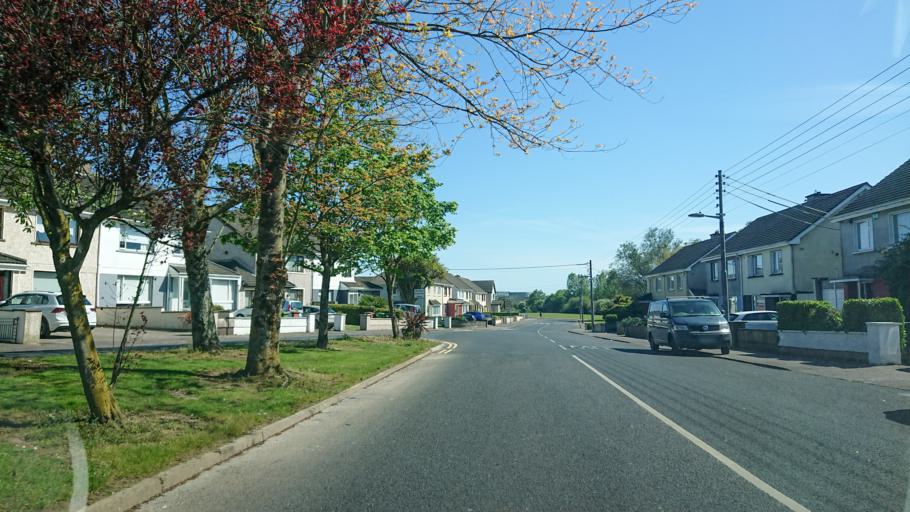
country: IE
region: Munster
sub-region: Waterford
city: Waterford
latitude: 52.2503
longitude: -7.1443
